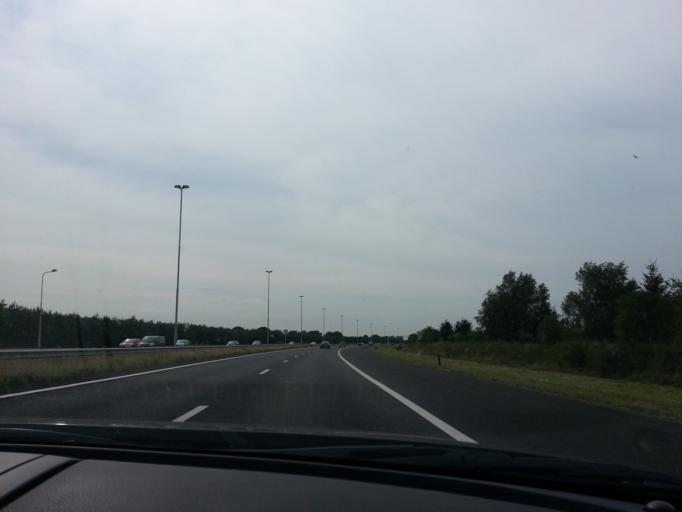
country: NL
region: North Brabant
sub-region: Gemeente Goirle
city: Goirle
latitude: 51.5383
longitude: 4.9988
